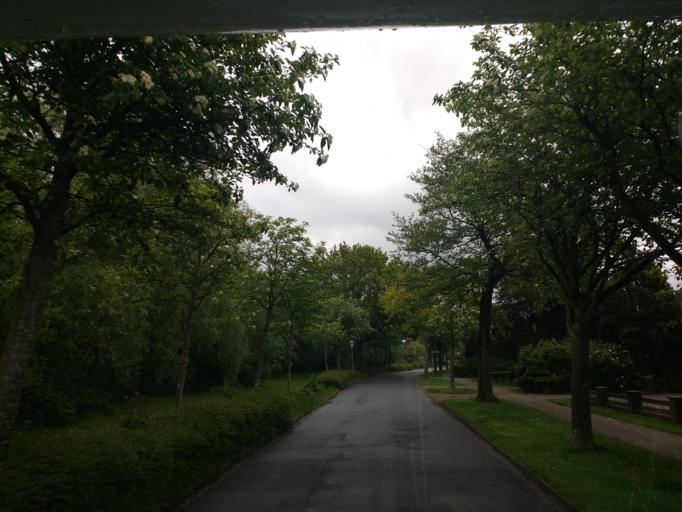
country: DE
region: Lower Saxony
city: Schillig
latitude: 53.7048
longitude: 8.0207
